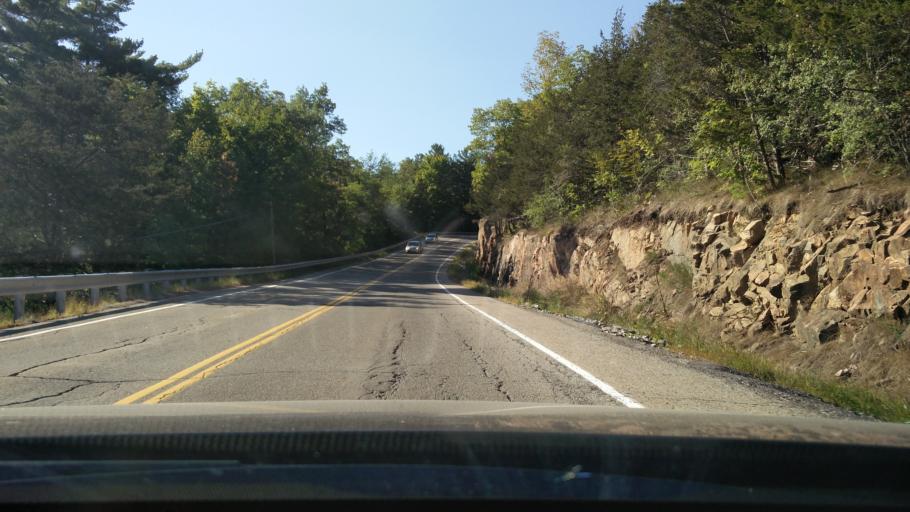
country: CA
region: Ontario
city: Perth
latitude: 44.6842
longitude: -76.3960
